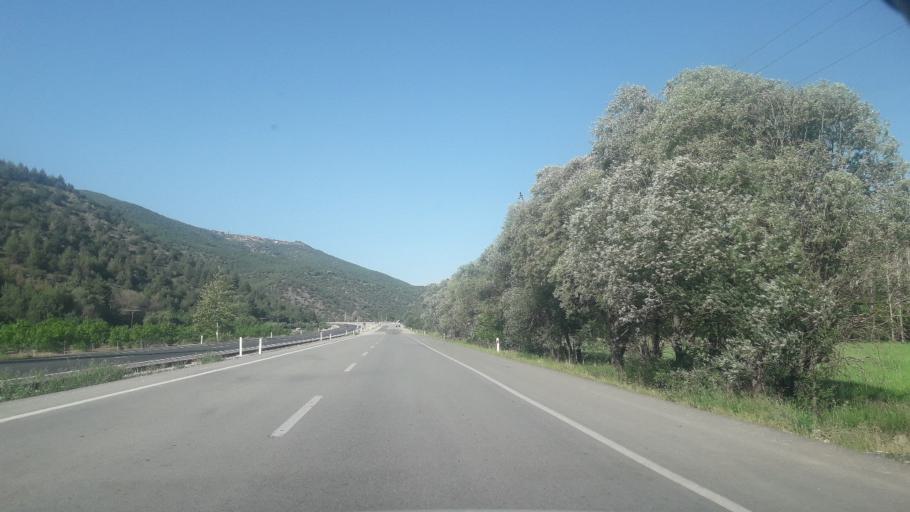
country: TR
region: Tokat
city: Turhal
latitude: 40.4762
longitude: 36.1490
